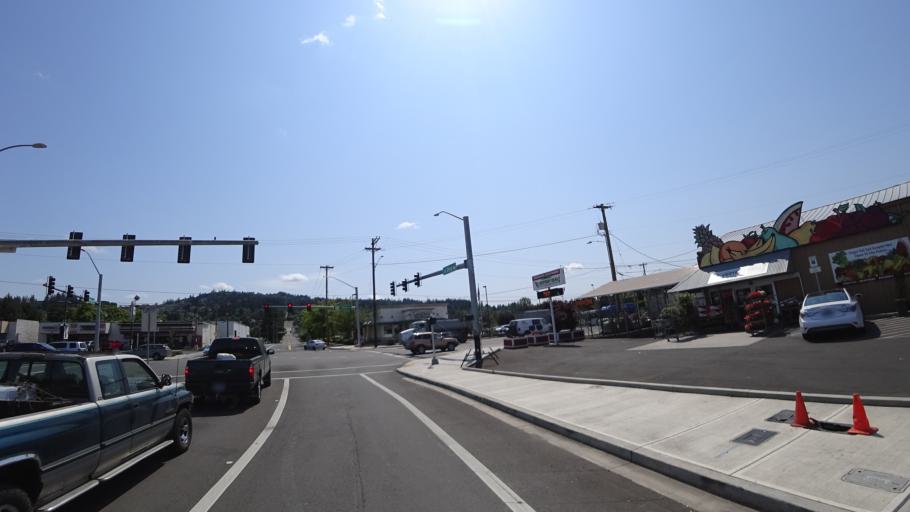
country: US
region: Oregon
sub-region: Multnomah County
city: Lents
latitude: 45.4515
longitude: -122.5796
